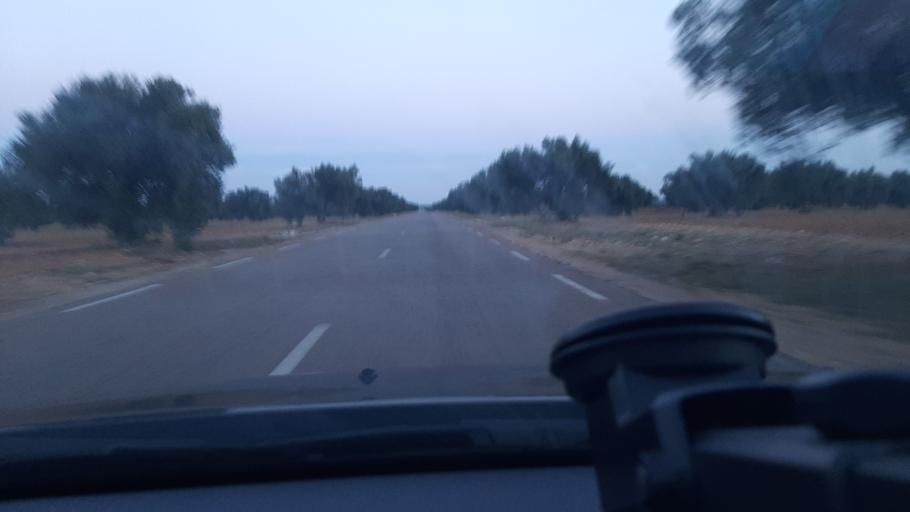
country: TN
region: Al Mahdiyah
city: Shurban
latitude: 35.0323
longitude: 10.5033
